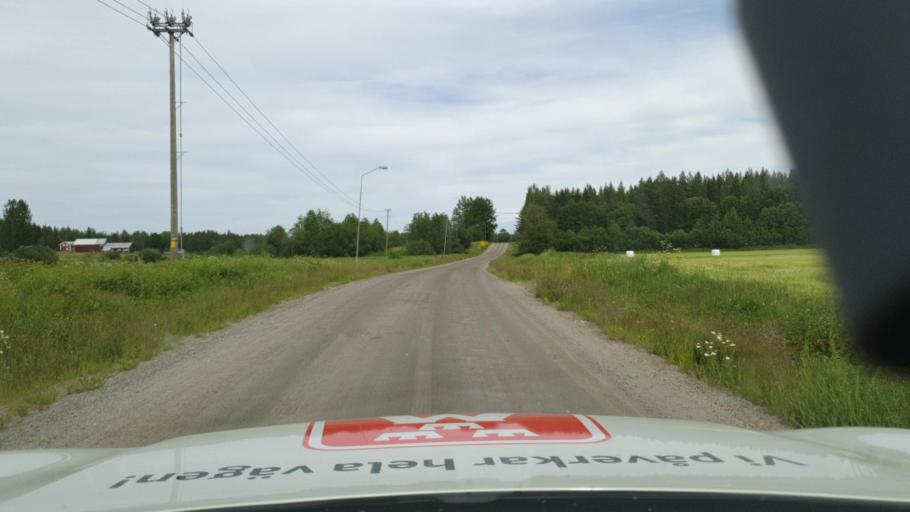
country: SE
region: Vaesterbotten
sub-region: Skelleftea Kommun
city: Viken
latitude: 64.5130
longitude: 20.9440
